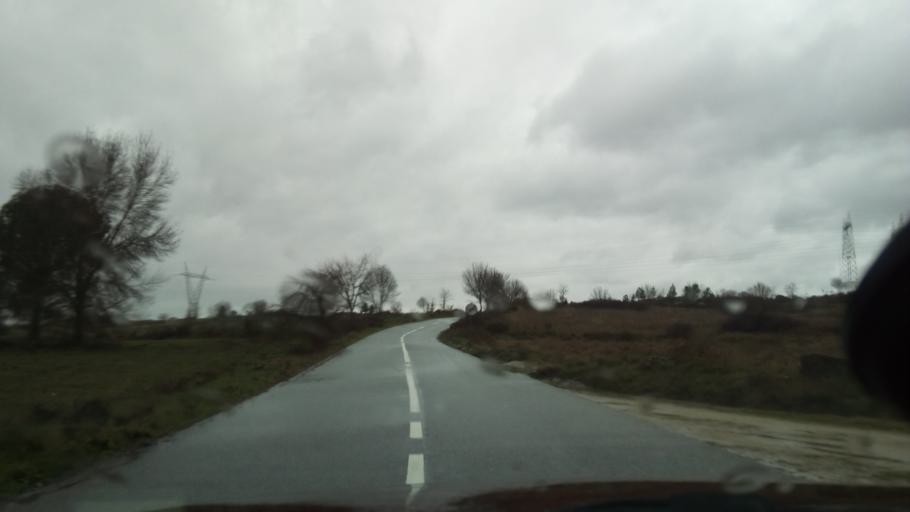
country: PT
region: Guarda
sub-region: Fornos de Algodres
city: Fornos de Algodres
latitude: 40.5751
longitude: -7.5075
